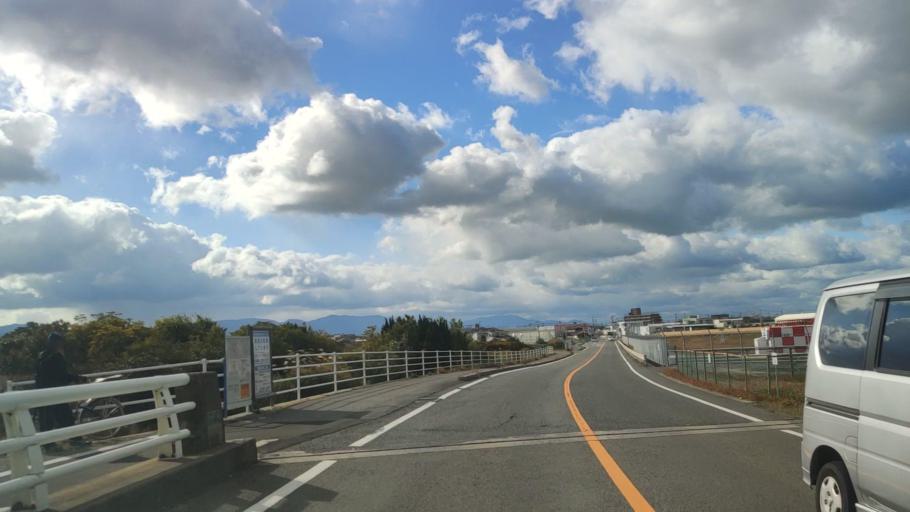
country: JP
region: Ehime
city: Masaki-cho
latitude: 33.8192
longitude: 132.7129
